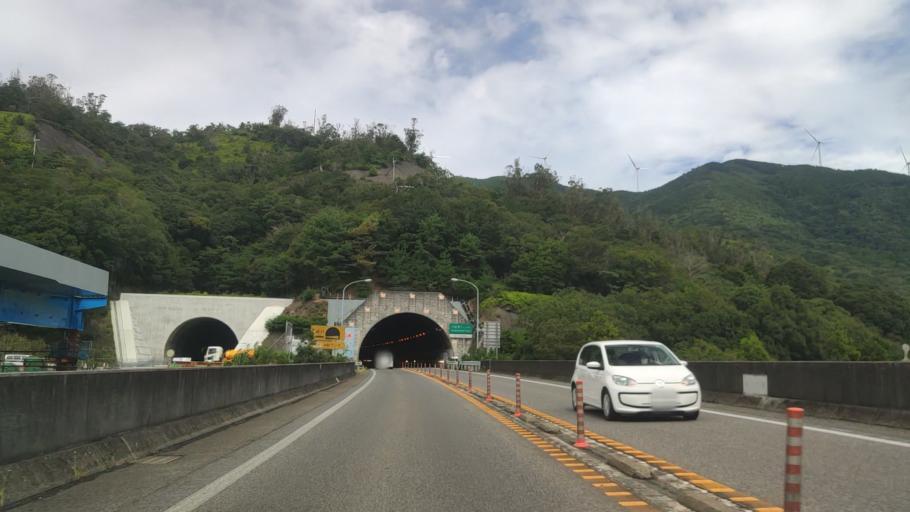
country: JP
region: Wakayama
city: Gobo
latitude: 33.9426
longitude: 135.1986
